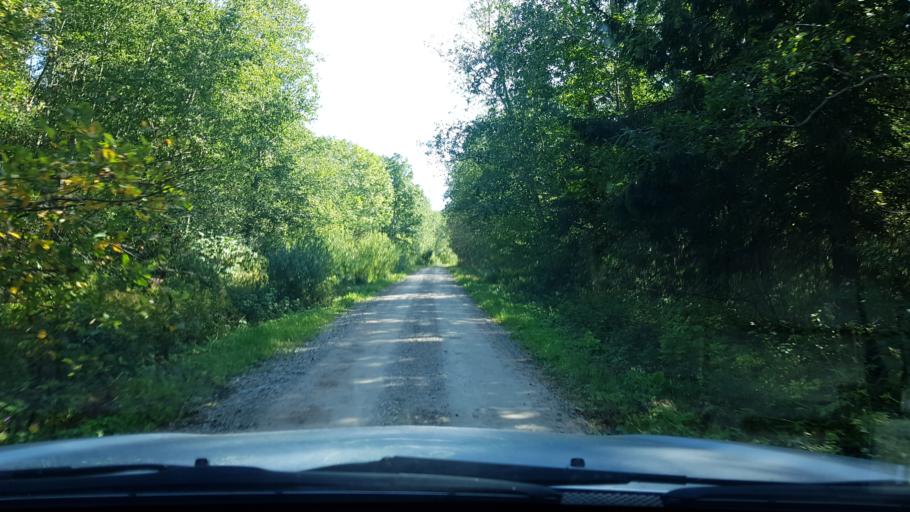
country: EE
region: Ida-Virumaa
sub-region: Sillamaee linn
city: Sillamae
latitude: 59.3321
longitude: 27.7668
